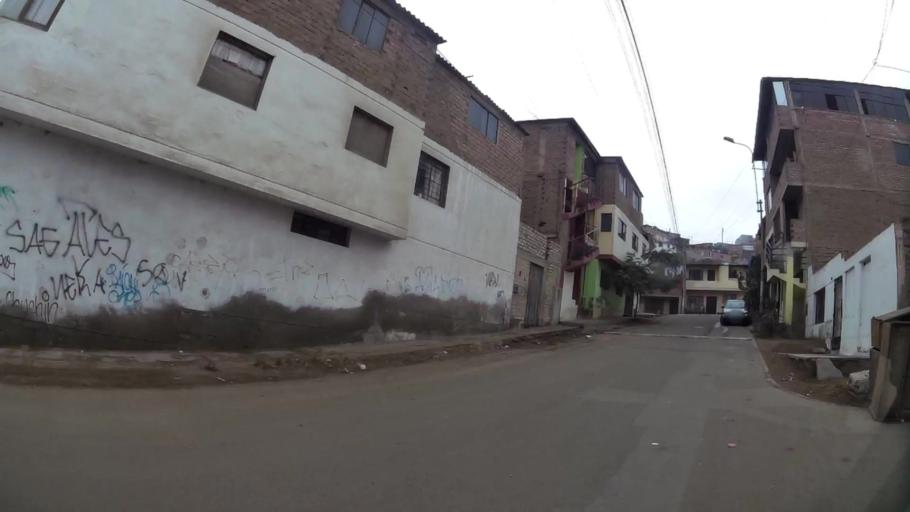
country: PE
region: Lima
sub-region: Lima
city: Surco
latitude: -12.1687
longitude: -76.9534
